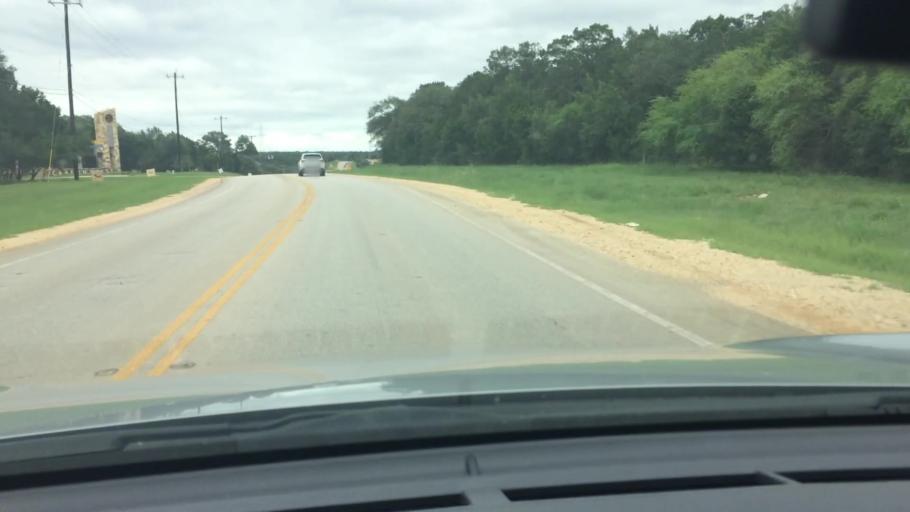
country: US
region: Texas
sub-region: Comal County
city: Garden Ridge
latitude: 29.6428
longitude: -98.3899
